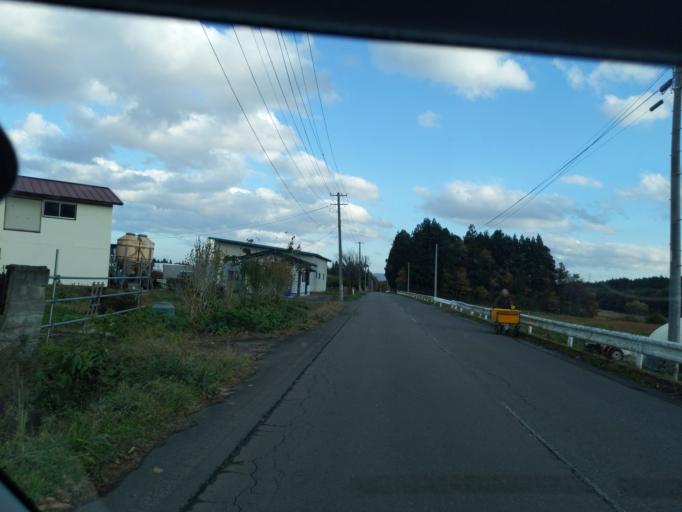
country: JP
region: Iwate
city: Mizusawa
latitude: 39.0999
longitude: 140.9991
